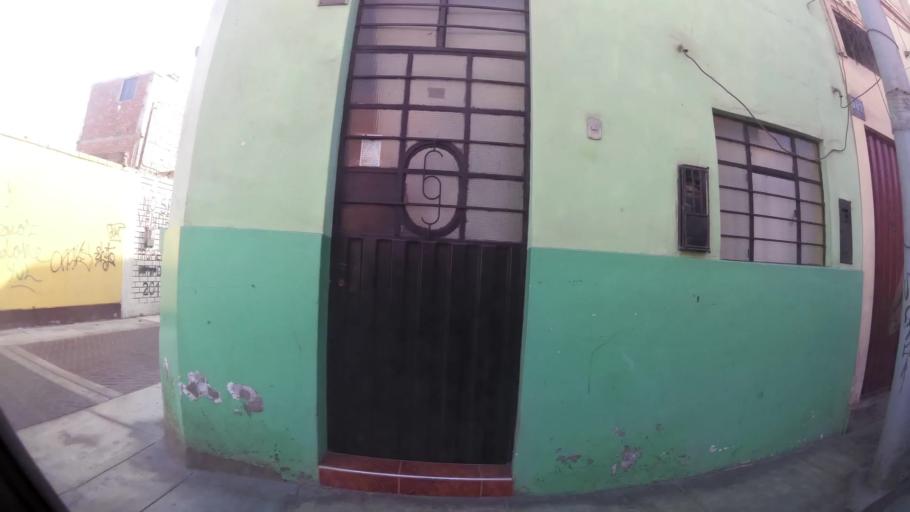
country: PE
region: Lima
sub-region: Huaura
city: Huacho
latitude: -11.1107
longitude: -77.6107
